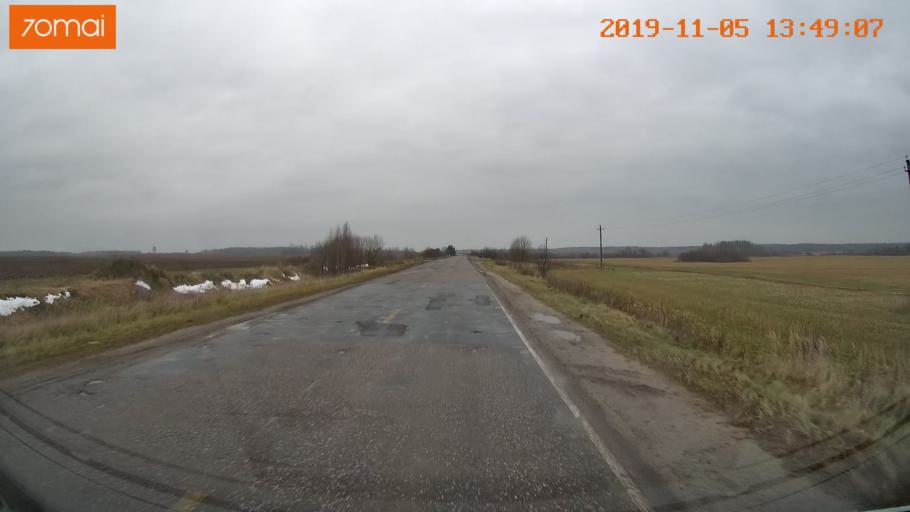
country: RU
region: Ivanovo
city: Kaminskiy
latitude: 57.0076
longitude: 41.4083
